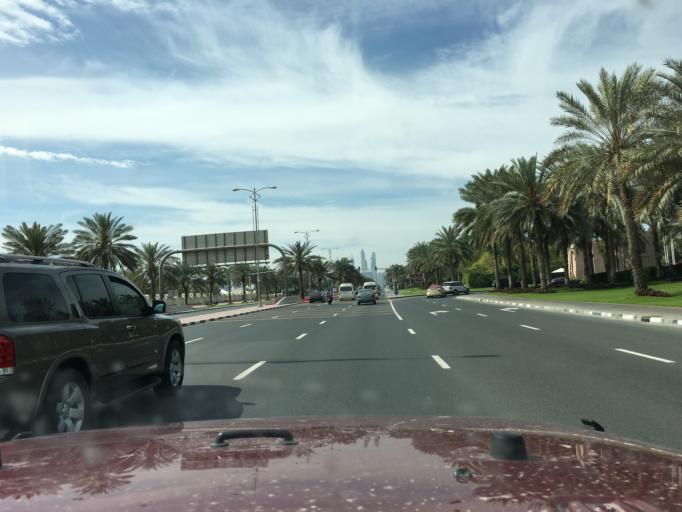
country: AE
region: Dubai
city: Dubai
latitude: 25.1313
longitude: 55.1870
